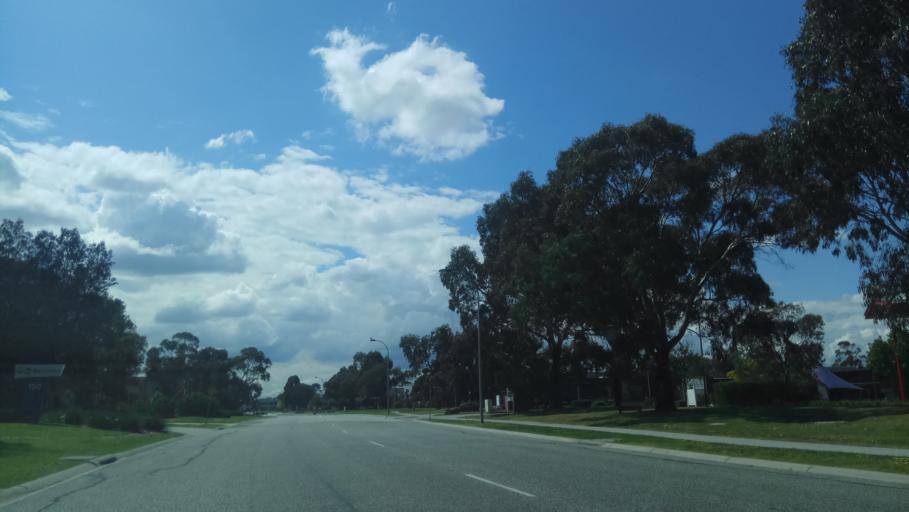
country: AU
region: Victoria
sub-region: Kingston
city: Waterways
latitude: -38.0000
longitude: 145.1186
